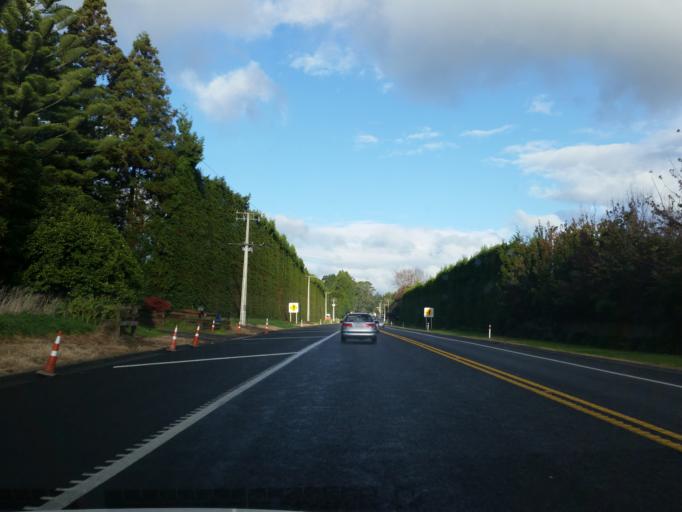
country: NZ
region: Bay of Plenty
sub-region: Western Bay of Plenty District
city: Katikati
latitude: -37.6230
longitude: 175.9531
